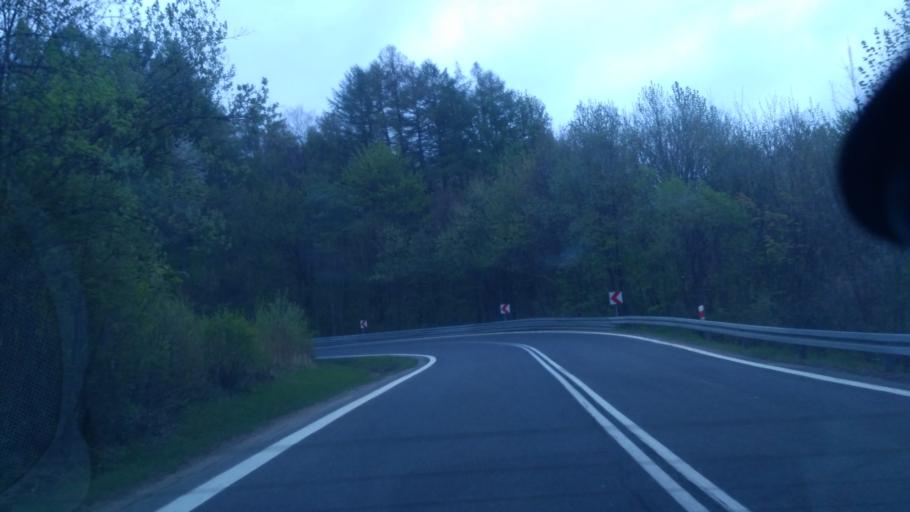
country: PL
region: Subcarpathian Voivodeship
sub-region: Powiat sanocki
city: Tyrawa Woloska
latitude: 49.5571
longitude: 22.3269
